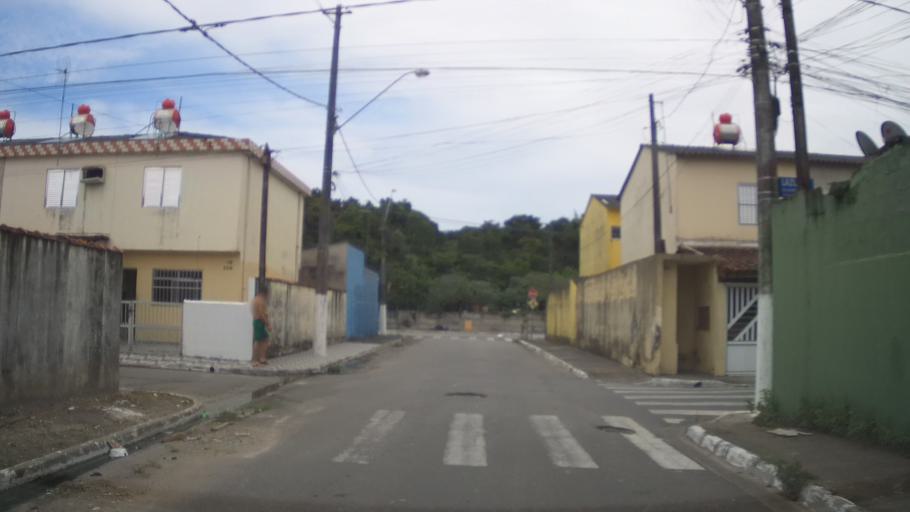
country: BR
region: Sao Paulo
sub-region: Praia Grande
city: Praia Grande
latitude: -24.0235
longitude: -46.5017
